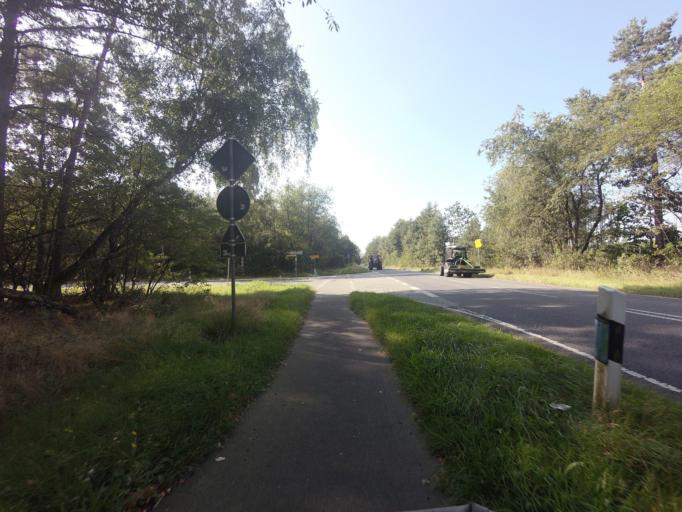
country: DE
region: Lower Saxony
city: Wielen
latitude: 52.5235
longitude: 6.7411
